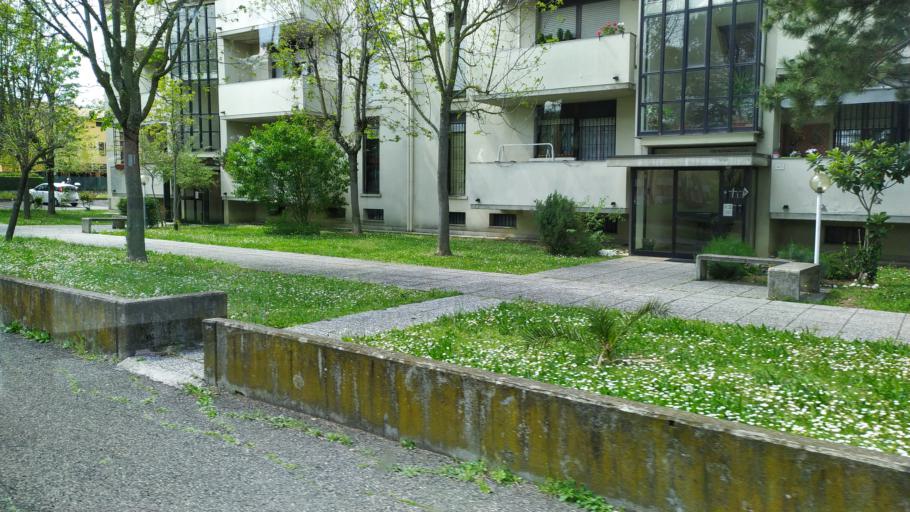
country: IT
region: Emilia-Romagna
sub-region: Provincia di Bologna
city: Imola
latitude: 44.3430
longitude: 11.6794
